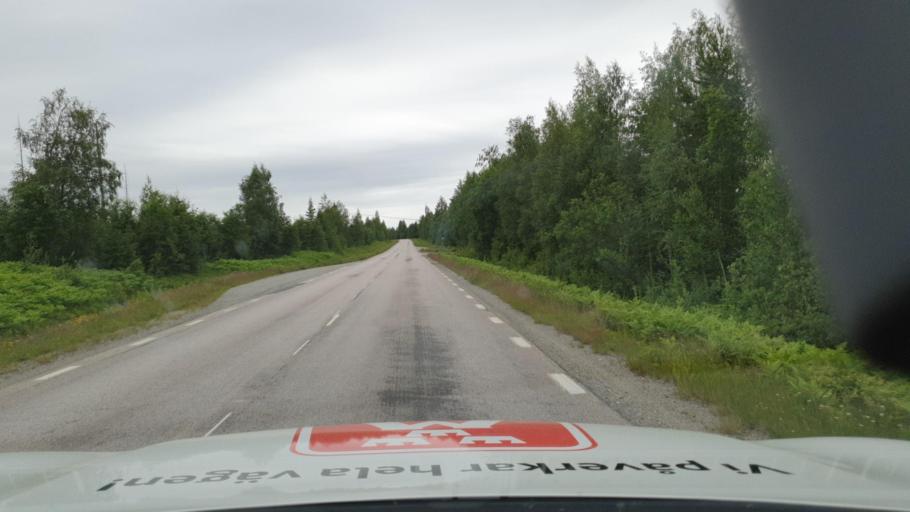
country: SE
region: Vaesterbotten
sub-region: Vannas Kommun
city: Vaennaes
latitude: 63.7930
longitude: 19.8140
